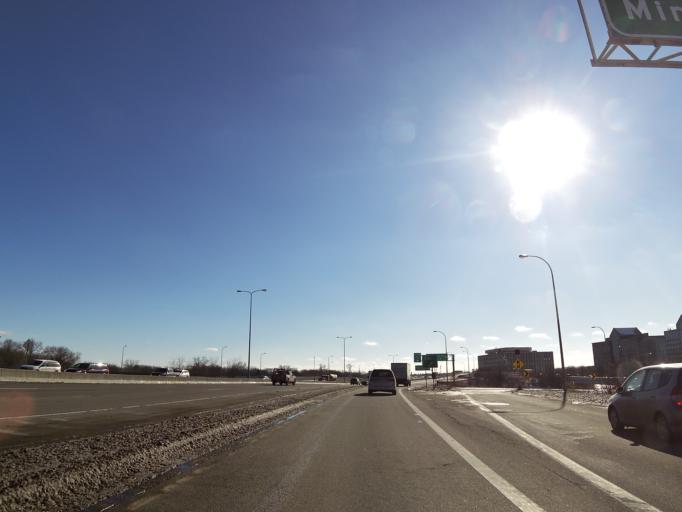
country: US
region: Minnesota
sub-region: Hennepin County
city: Saint Louis Park
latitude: 44.9703
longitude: -93.3413
